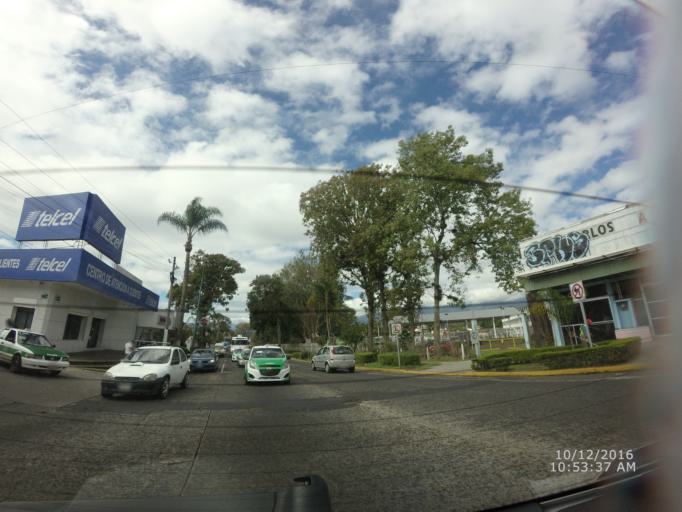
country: TR
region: Sivas
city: Karayun
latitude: 39.6719
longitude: 37.2423
